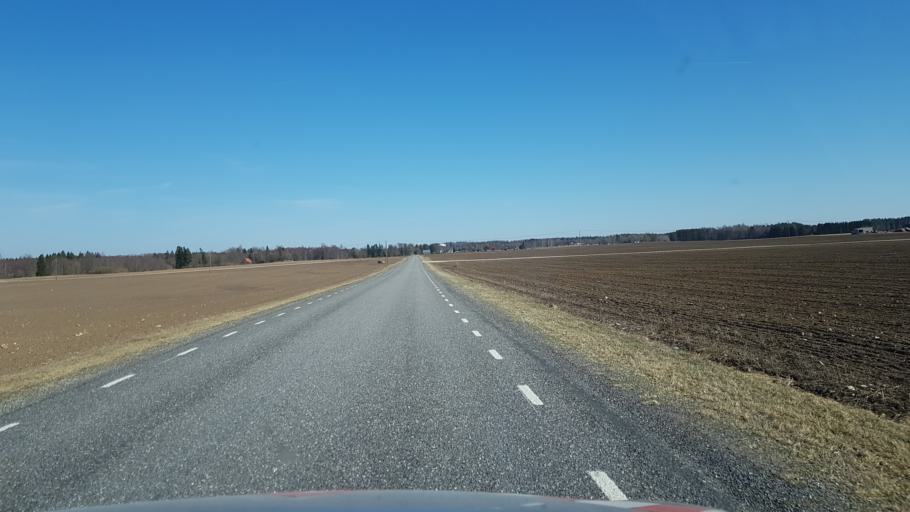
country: EE
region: Laeaene-Virumaa
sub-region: Rakke vald
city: Rakke
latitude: 59.0057
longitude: 26.1819
